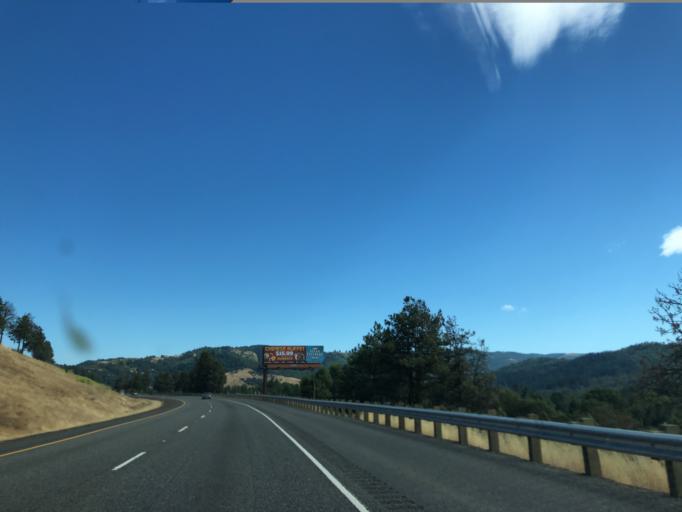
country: US
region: Oregon
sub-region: Douglas County
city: Winston
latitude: 43.0807
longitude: -123.3651
